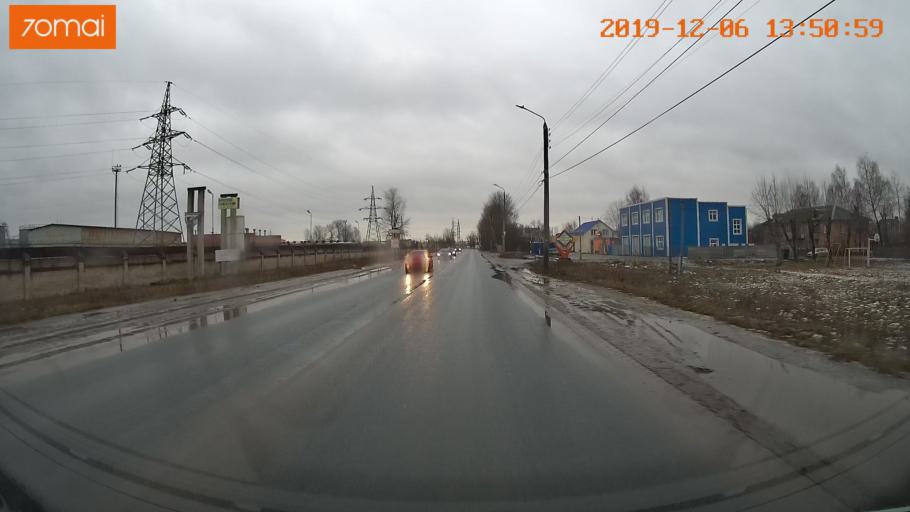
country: RU
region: Ivanovo
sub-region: Gorod Ivanovo
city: Ivanovo
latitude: 56.9718
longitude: 40.9540
